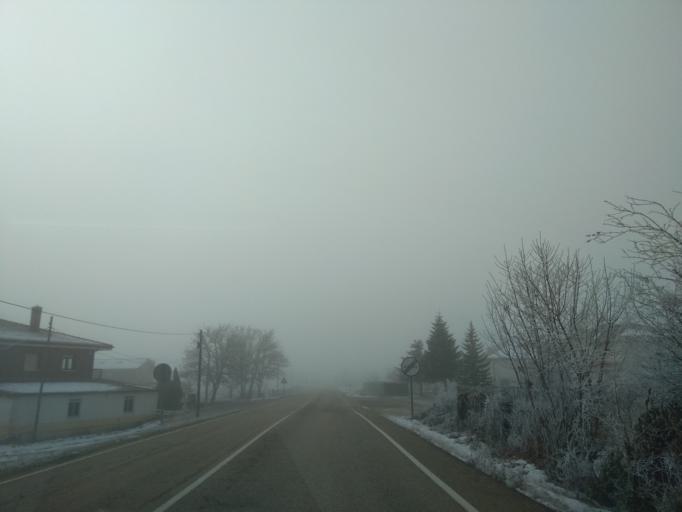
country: ES
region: Castille and Leon
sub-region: Provincia de Burgos
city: Espinosa de los Monteros
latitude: 43.0404
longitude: -3.4931
